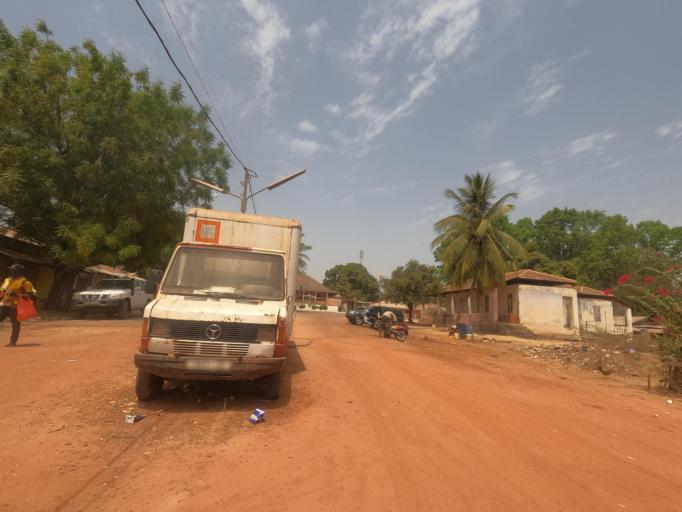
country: GW
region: Cacheu
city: Cacheu
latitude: 12.4003
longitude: -16.1964
